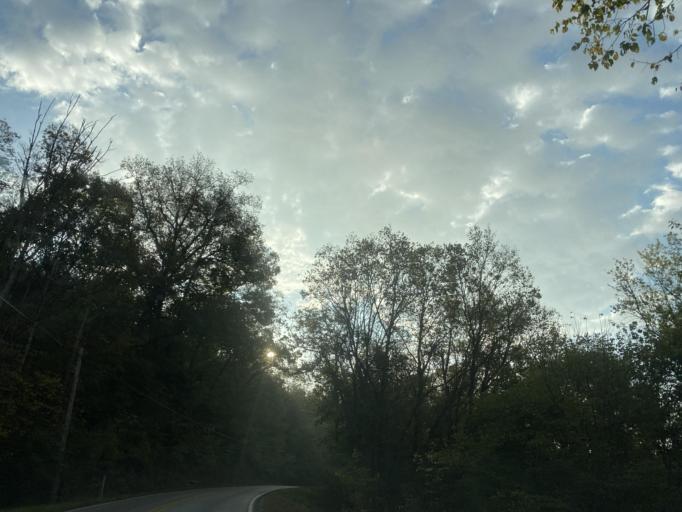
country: US
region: Kentucky
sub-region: Pendleton County
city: Falmouth
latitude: 38.7897
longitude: -84.3398
